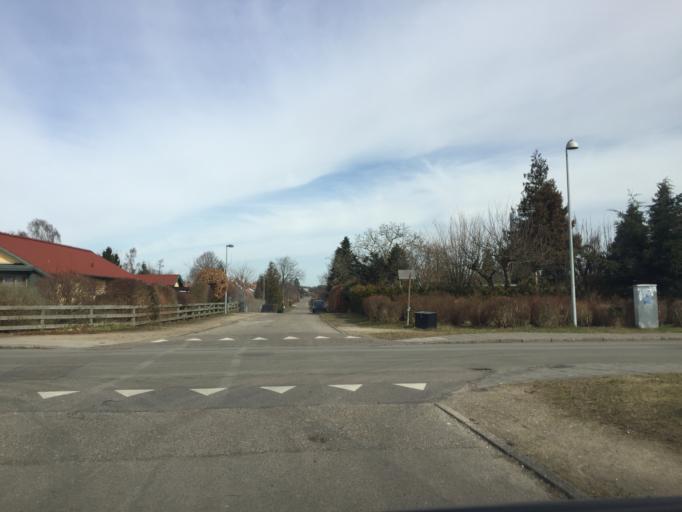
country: DK
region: Capital Region
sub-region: Fureso Kommune
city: Farum
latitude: 55.8126
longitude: 12.3639
